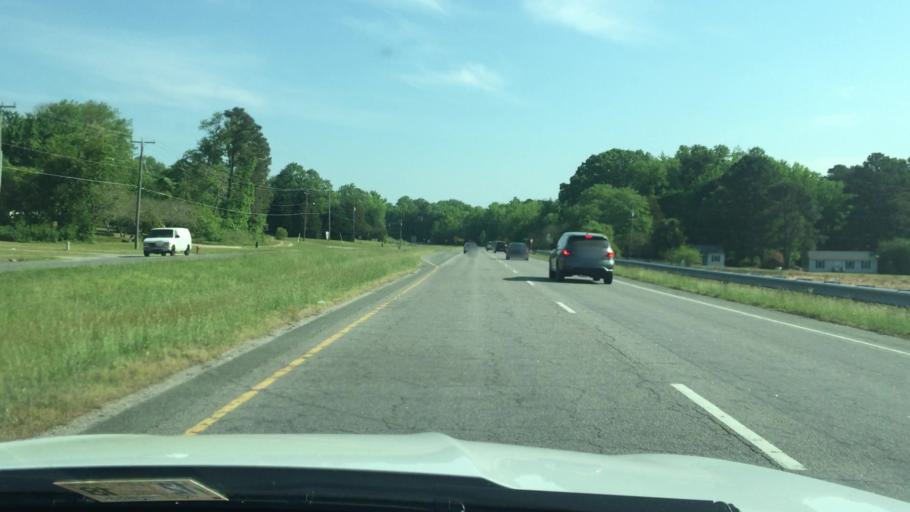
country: US
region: Virginia
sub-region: Lancaster County
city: Kilmarnock
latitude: 37.6935
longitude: -76.3747
